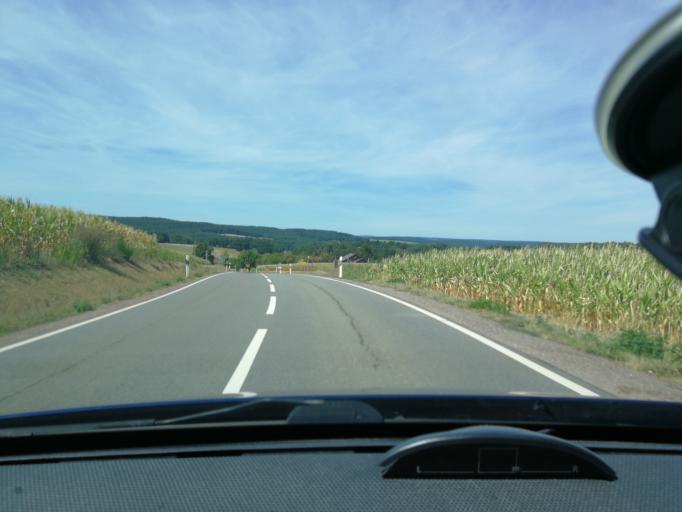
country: DE
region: Rheinland-Pfalz
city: Niersbach
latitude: 49.9298
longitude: 6.7561
